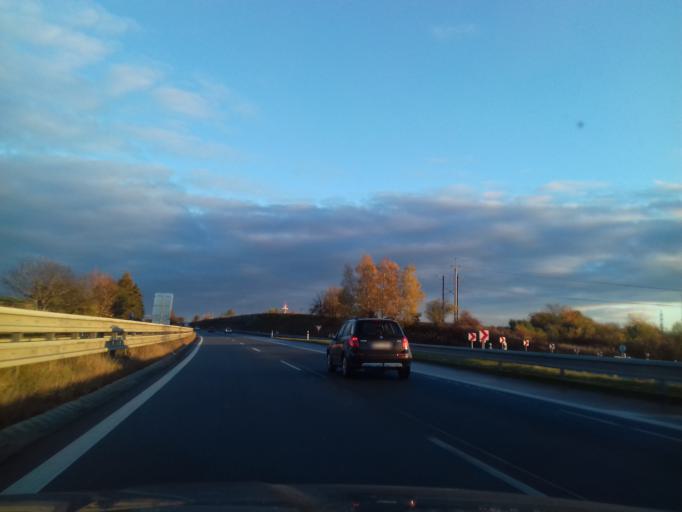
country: CZ
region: Olomoucky
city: Otaslavice
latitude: 49.3703
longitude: 17.0977
